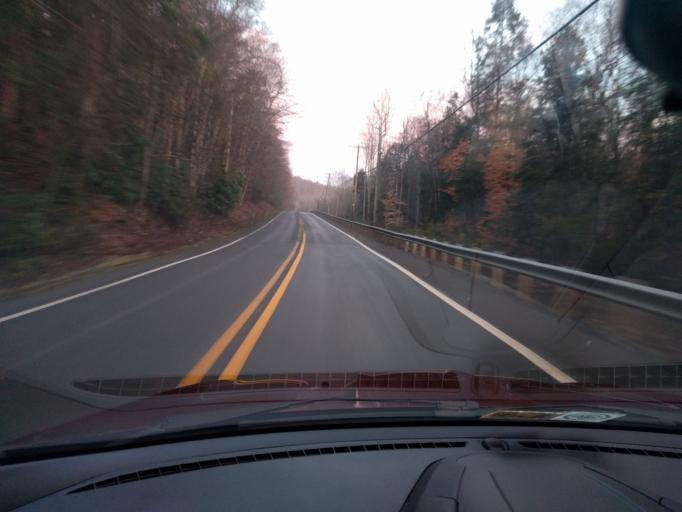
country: US
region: West Virginia
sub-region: Greenbrier County
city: Rainelle
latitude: 38.0361
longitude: -80.9186
